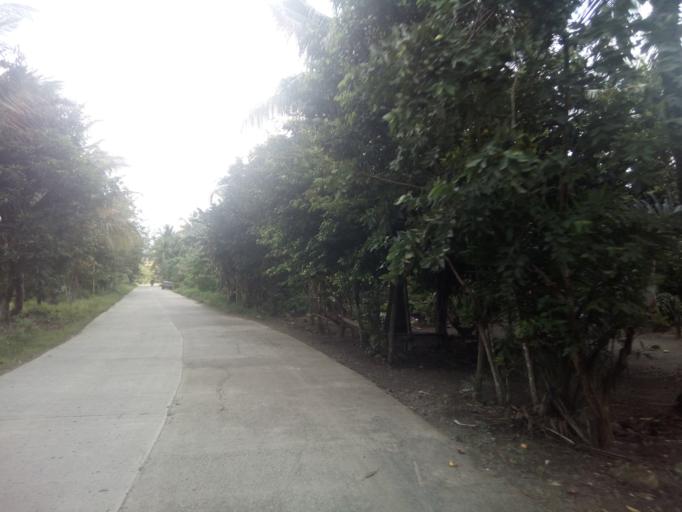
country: PH
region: Caraga
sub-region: Province of Agusan del Sur
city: Santa Josefa
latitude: 7.9925
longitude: 126.0301
